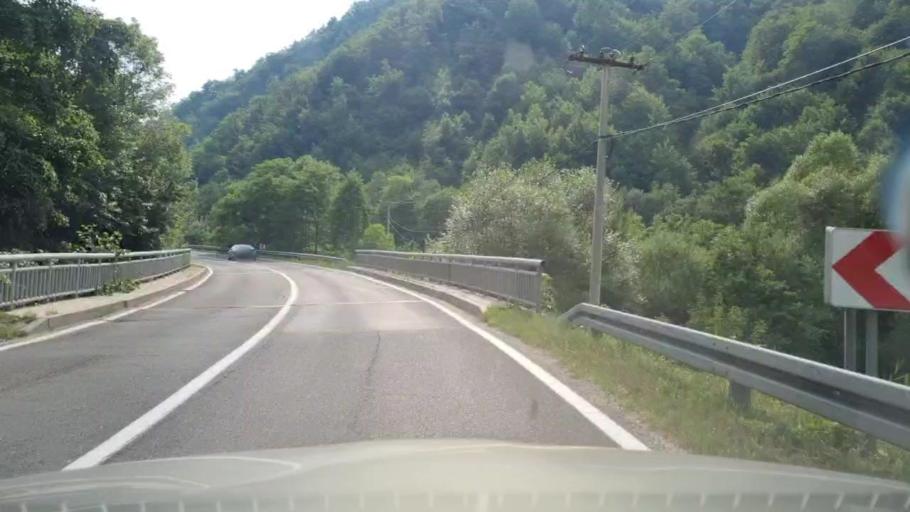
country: BA
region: Federation of Bosnia and Herzegovina
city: Vogosca
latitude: 43.9748
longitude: 18.3759
